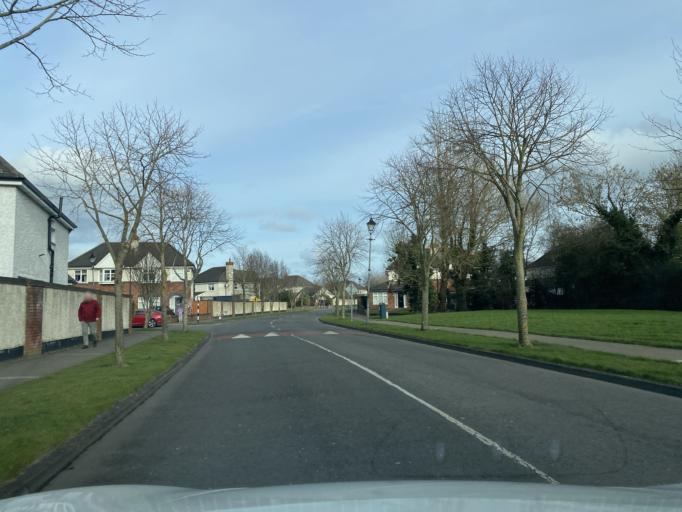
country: IE
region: Leinster
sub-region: Kildare
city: Celbridge
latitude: 53.3379
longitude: -6.5535
